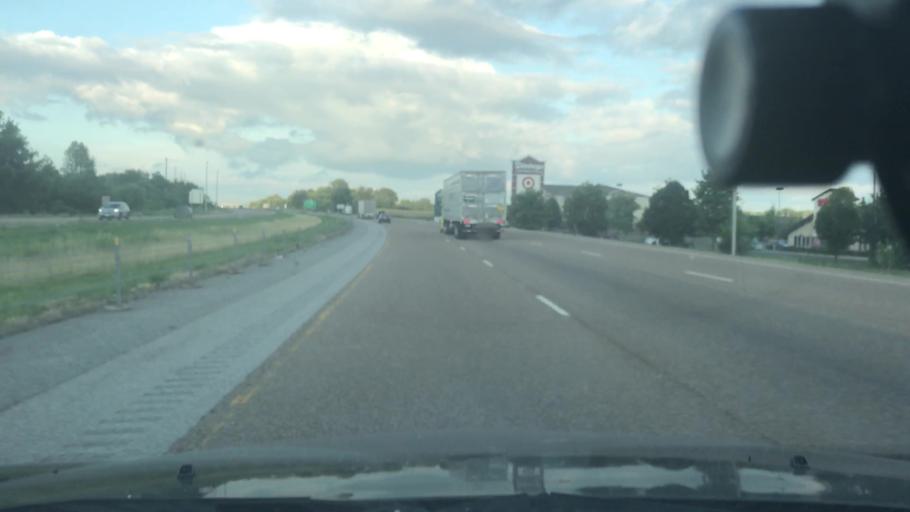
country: US
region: Illinois
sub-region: Saint Clair County
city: O'Fallon
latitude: 38.5749
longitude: -89.9248
